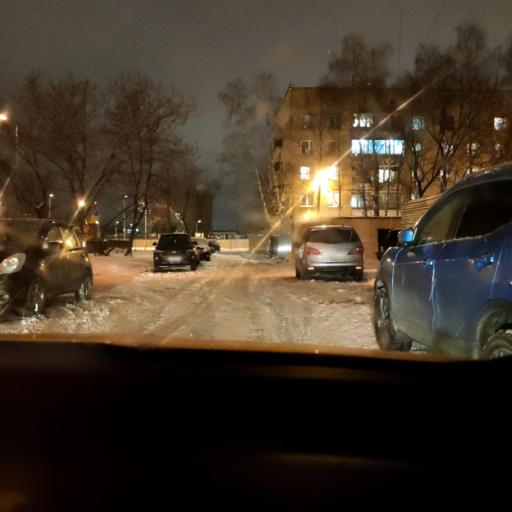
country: RU
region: Moskovskaya
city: Khoroshevo-Mnevniki
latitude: 55.7913
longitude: 37.4759
